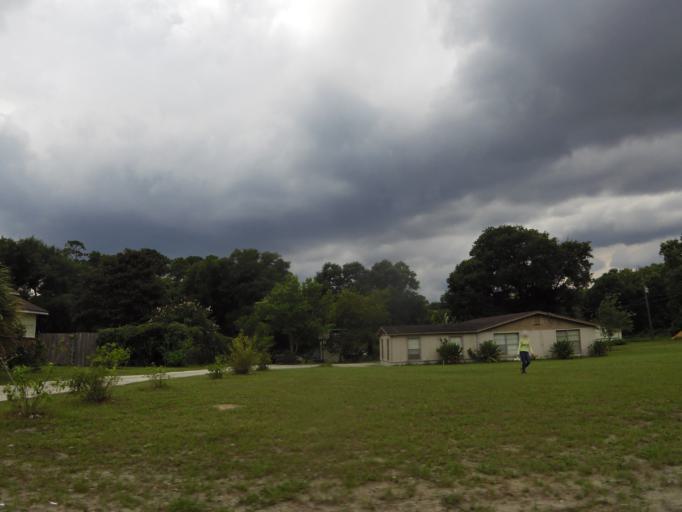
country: US
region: Florida
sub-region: Duval County
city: Jacksonville
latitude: 30.3330
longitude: -81.5372
